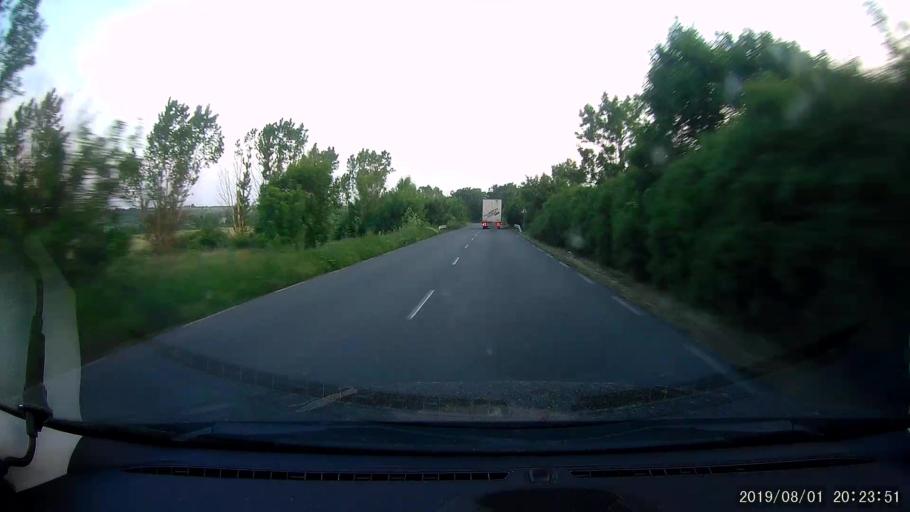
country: BG
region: Yambol
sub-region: Obshtina Elkhovo
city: Elkhovo
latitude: 42.2410
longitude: 26.5973
